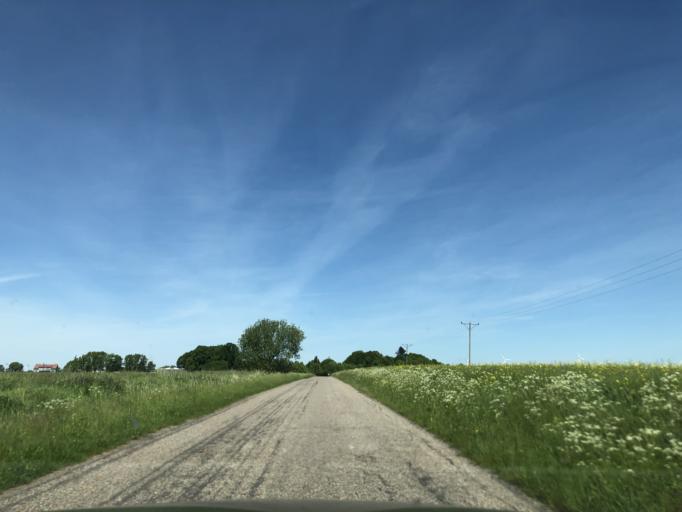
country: PL
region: West Pomeranian Voivodeship
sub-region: Powiat kolobrzeski
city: Goscino
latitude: 54.0038
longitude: 15.7193
